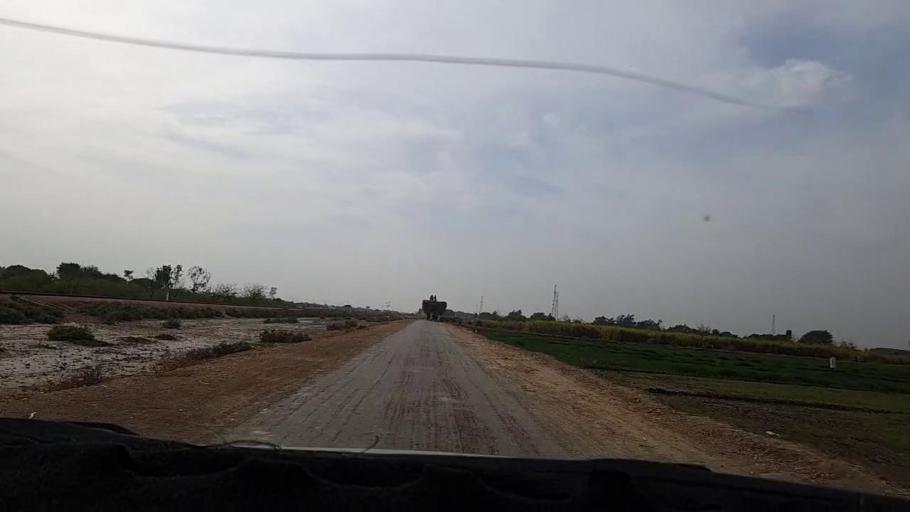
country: PK
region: Sindh
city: Pithoro
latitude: 25.5177
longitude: 69.2452
